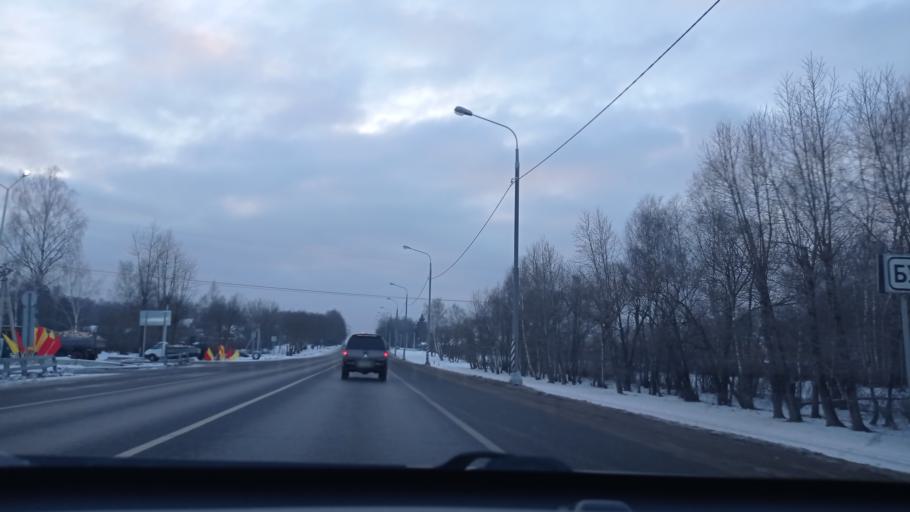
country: RU
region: Moskovskaya
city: Kievskij
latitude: 55.2390
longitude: 37.0431
